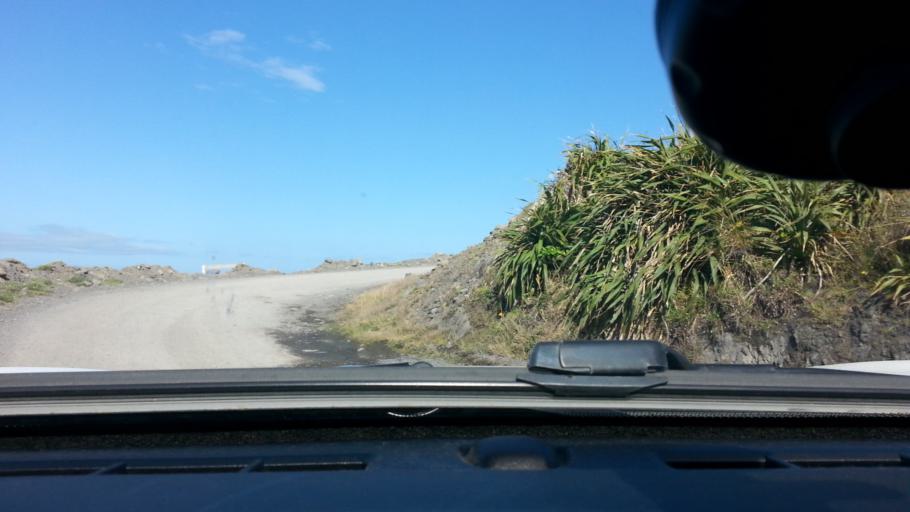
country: NZ
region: Wellington
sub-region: South Wairarapa District
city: Waipawa
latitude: -41.6044
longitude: 175.2638
